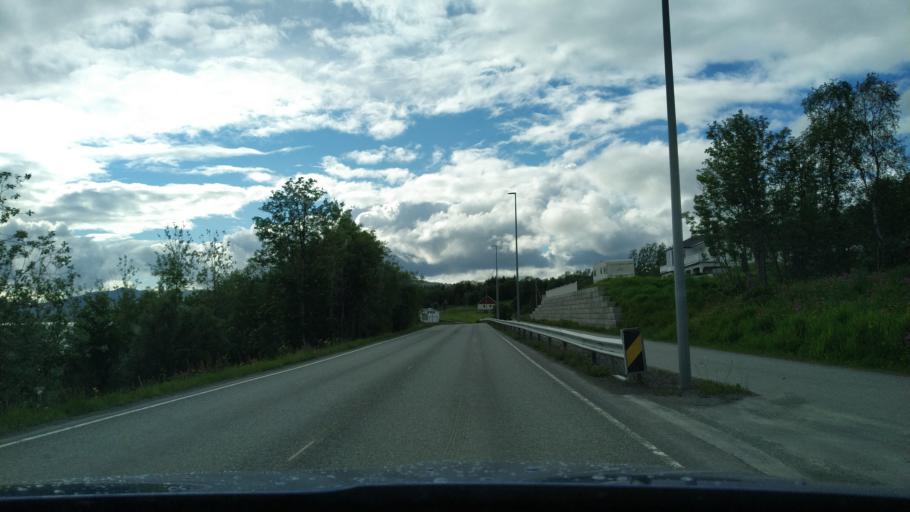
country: NO
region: Troms
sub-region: Sorreisa
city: Sorreisa
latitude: 69.1780
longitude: 18.0727
